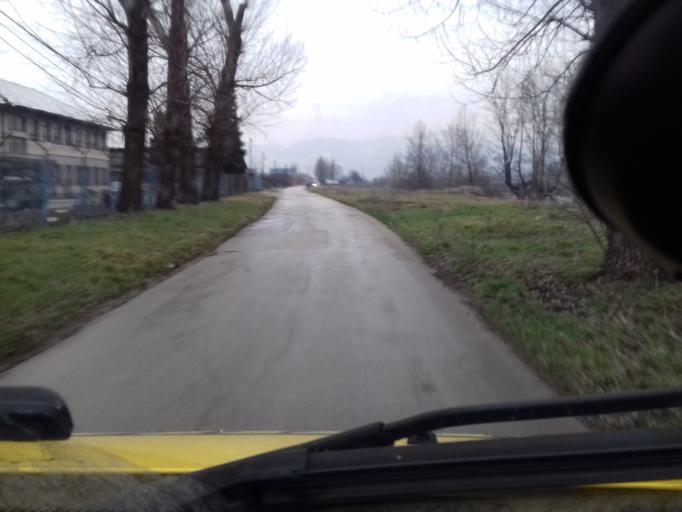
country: BA
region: Federation of Bosnia and Herzegovina
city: Zenica
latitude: 44.2250
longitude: 17.9071
